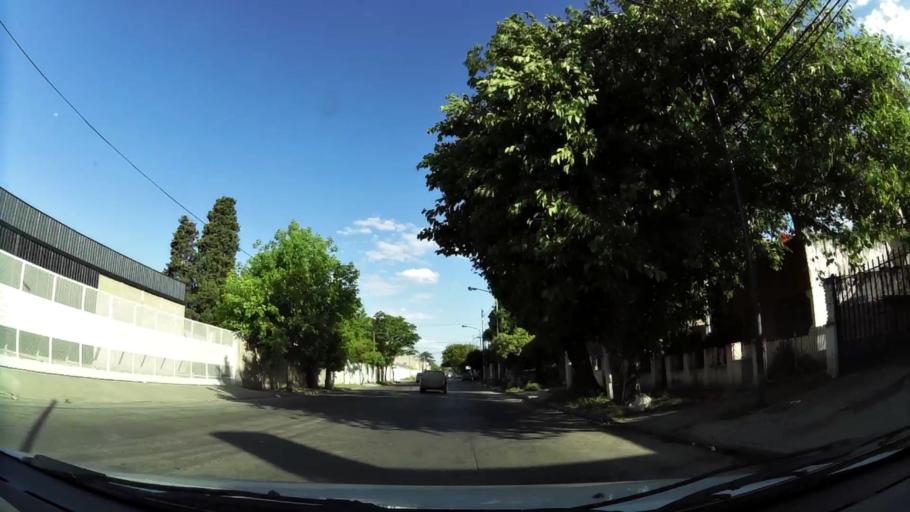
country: AR
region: Buenos Aires
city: Hurlingham
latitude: -34.5673
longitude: -58.6137
